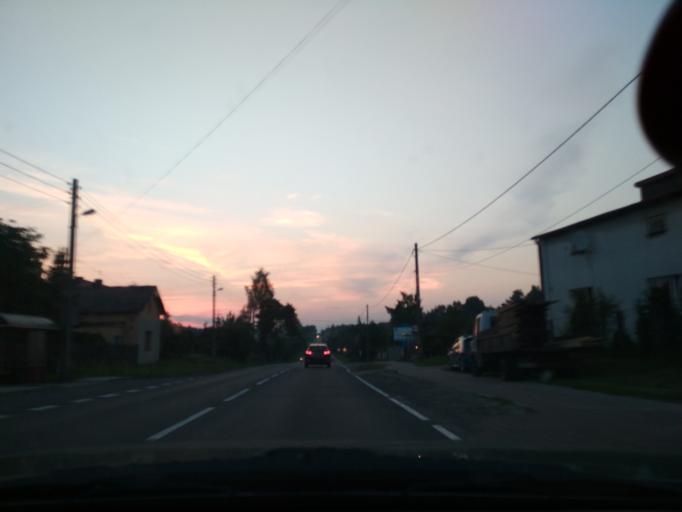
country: PL
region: Silesian Voivodeship
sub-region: Powiat zawiercianski
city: Ogrodzieniec
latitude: 50.4671
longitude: 19.4880
